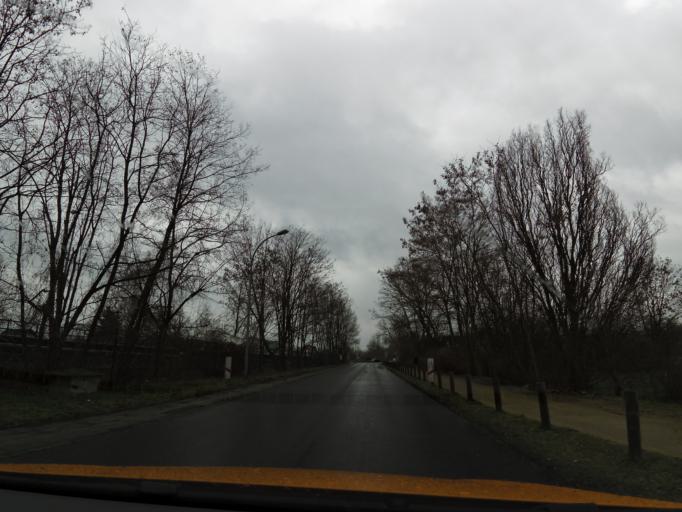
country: DE
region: Berlin
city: Lichtenrade
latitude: 52.3587
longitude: 13.4081
